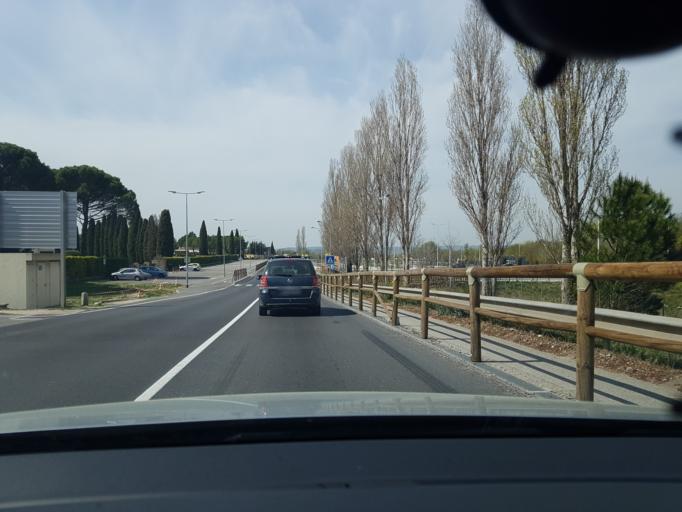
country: FR
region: Provence-Alpes-Cote d'Azur
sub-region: Departement des Bouches-du-Rhone
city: Bouc-Bel-Air
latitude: 43.4706
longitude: 5.4036
